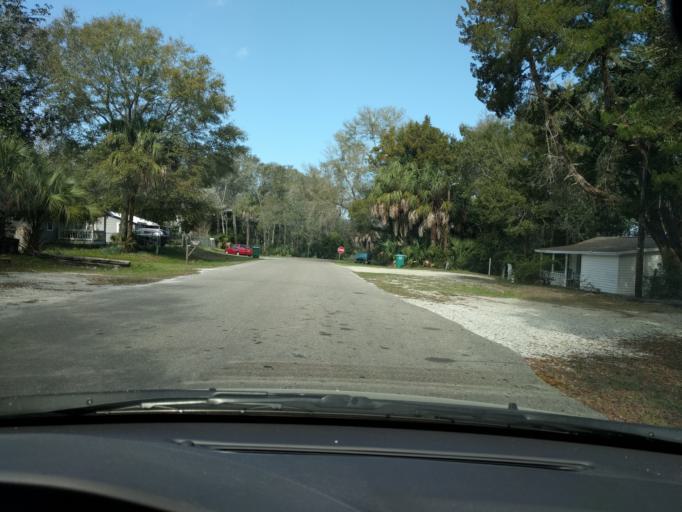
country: US
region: Florida
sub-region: Franklin County
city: Apalachicola
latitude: 29.7294
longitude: -84.9883
